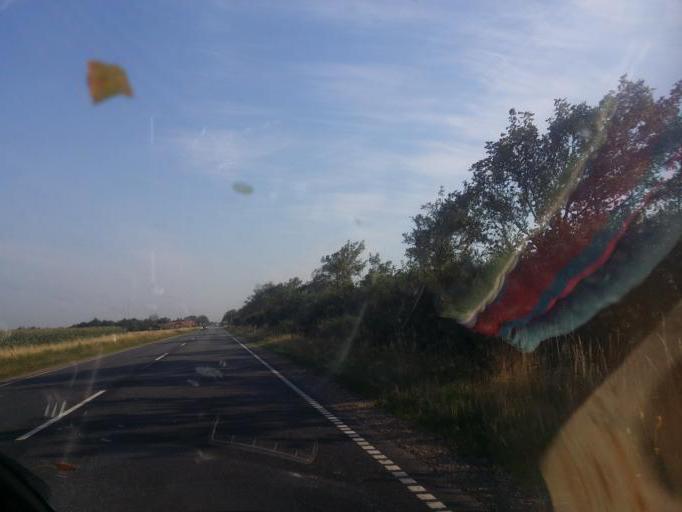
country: DK
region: South Denmark
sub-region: Tonder Kommune
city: Sherrebek
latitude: 55.2268
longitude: 8.7249
